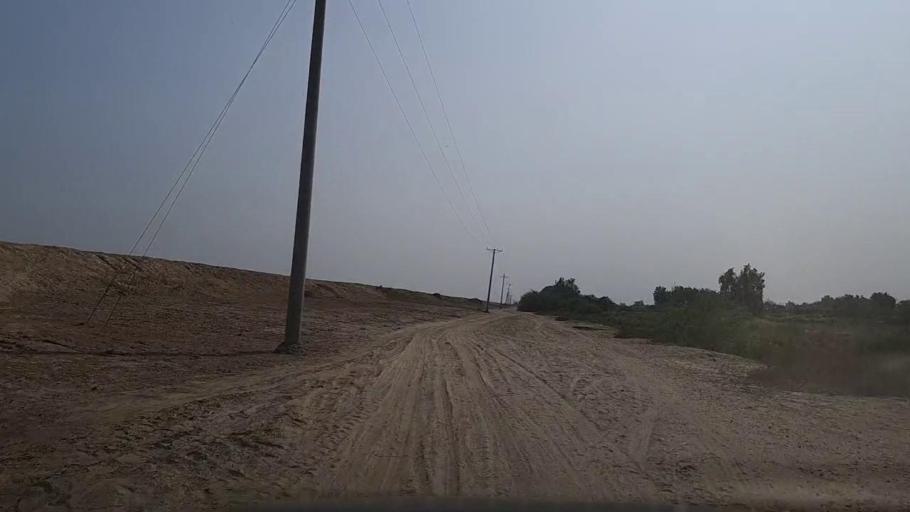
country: PK
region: Sindh
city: Thatta
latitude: 24.5620
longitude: 67.9136
